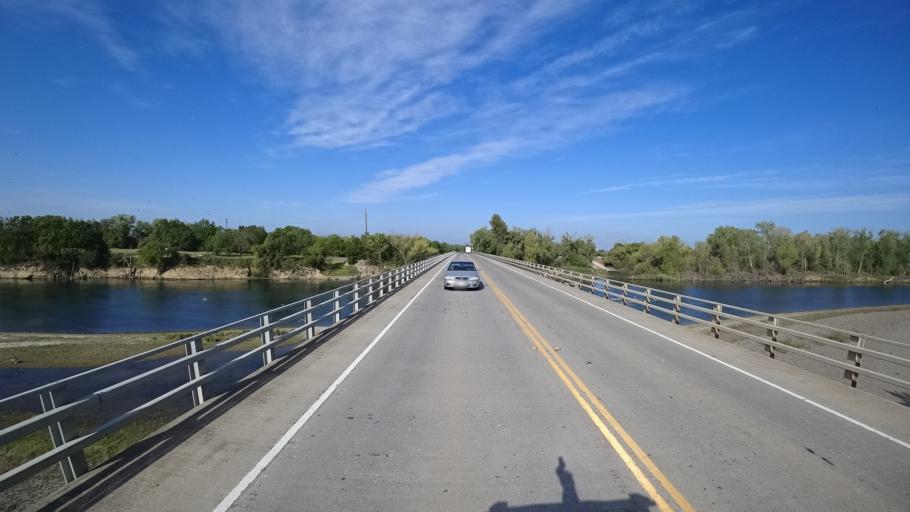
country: US
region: California
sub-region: Glenn County
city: Hamilton City
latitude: 39.6291
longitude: -121.9918
